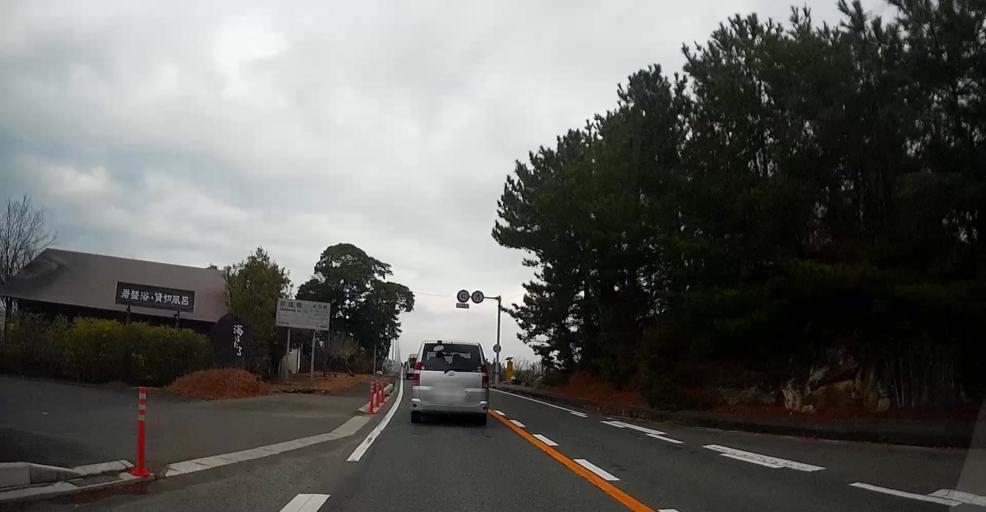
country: JP
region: Kumamoto
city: Yatsushiro
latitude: 32.5268
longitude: 130.4249
